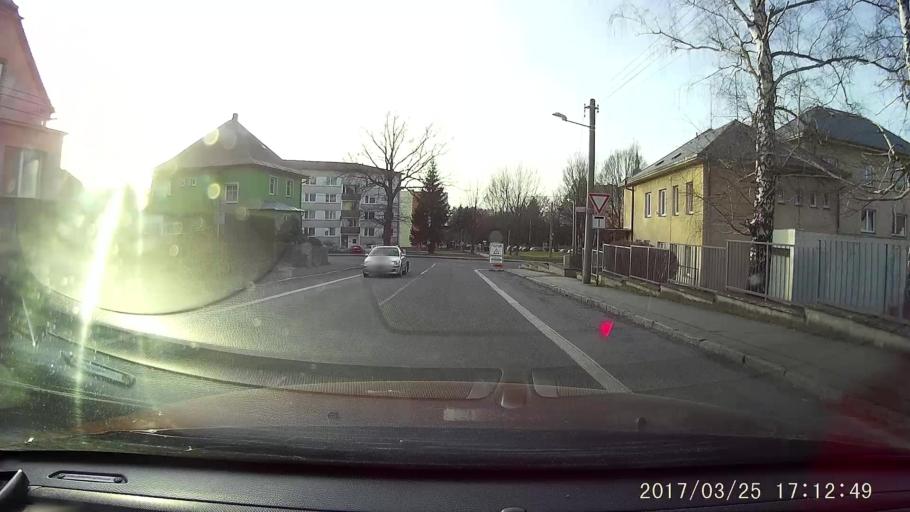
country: CZ
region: Liberecky
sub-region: Okres Liberec
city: Frydlant
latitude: 50.9247
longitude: 15.0889
